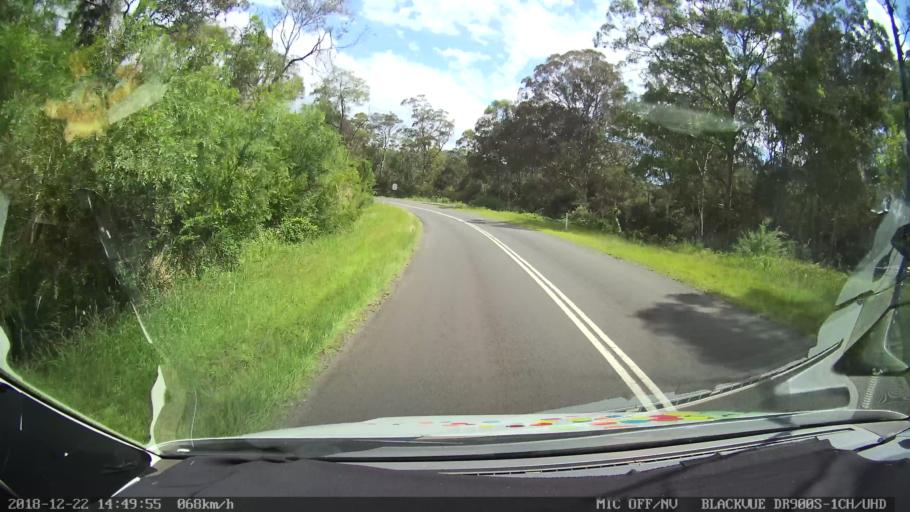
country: AU
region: New South Wales
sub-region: Bellingen
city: Dorrigo
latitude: -30.1909
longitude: 152.5422
